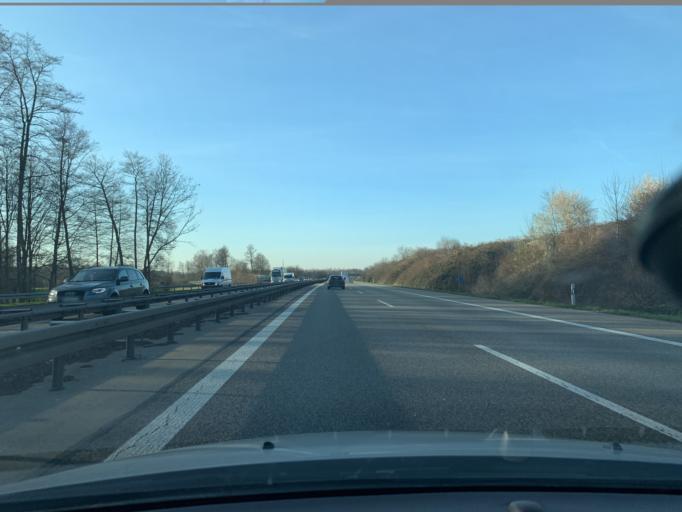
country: DE
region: Baden-Wuerttemberg
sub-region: Freiburg Region
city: Teningen
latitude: 48.0829
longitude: 7.8017
